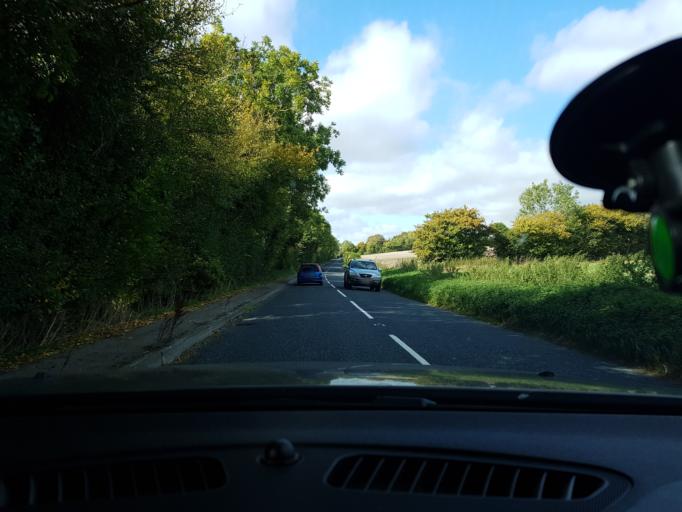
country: GB
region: England
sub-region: Wiltshire
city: Aldbourne
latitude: 51.4707
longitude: -1.6109
